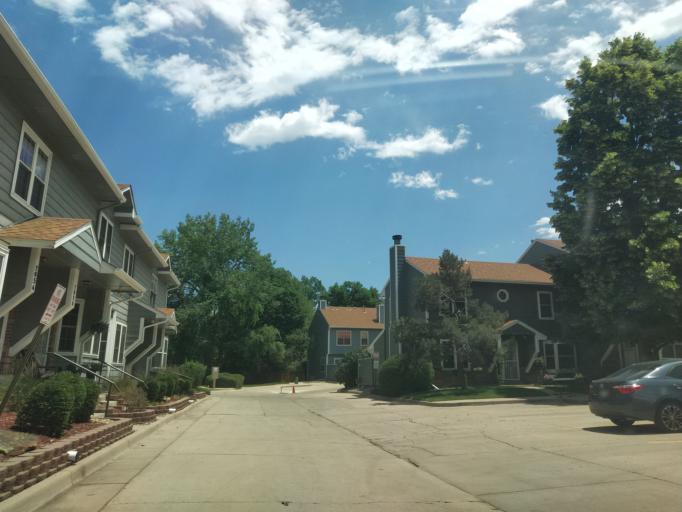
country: US
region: Colorado
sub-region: Jefferson County
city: Lakewood
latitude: 39.6810
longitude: -105.0874
